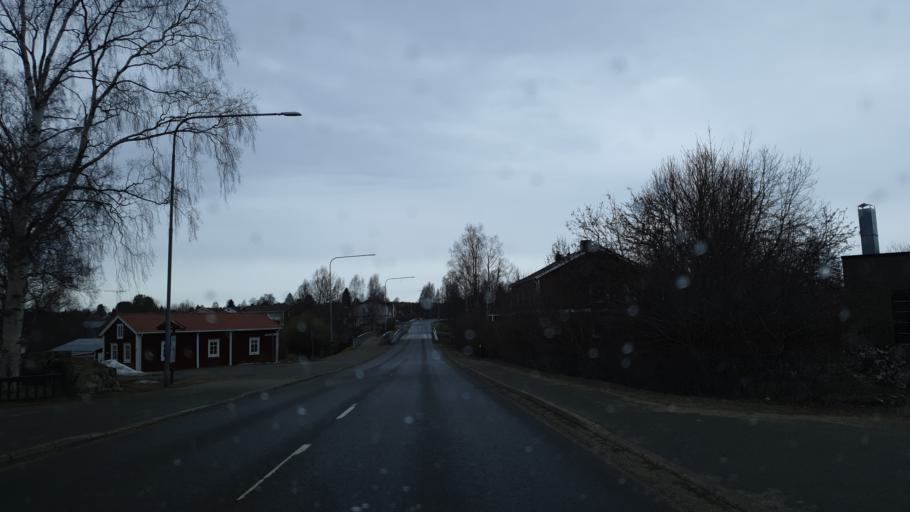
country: SE
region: Vaesterbotten
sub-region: Skelleftea Kommun
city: Kage
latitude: 64.8339
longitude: 20.9872
